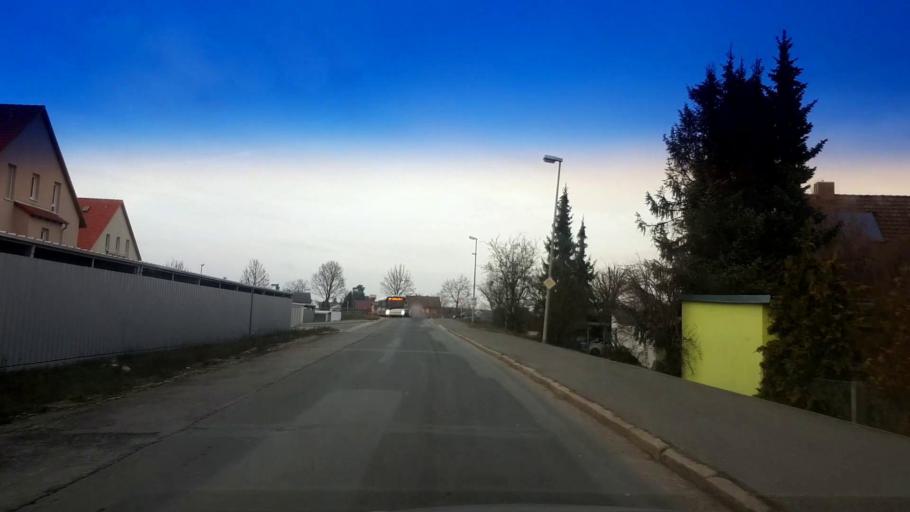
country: DE
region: Bavaria
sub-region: Upper Franconia
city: Hirschaid
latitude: 49.8097
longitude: 10.9812
